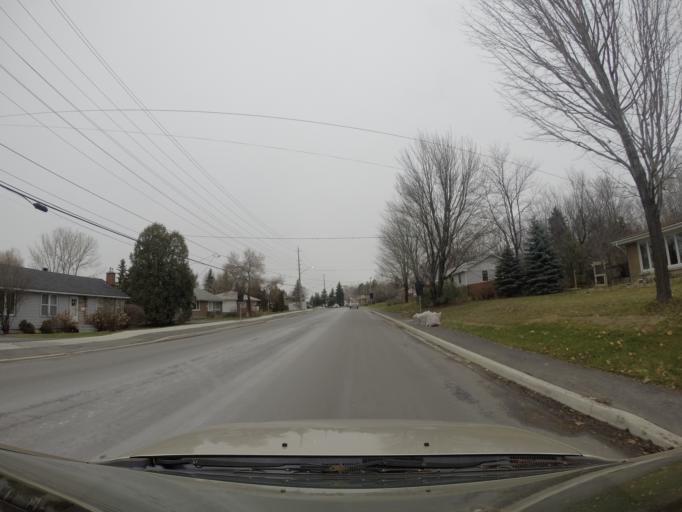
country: CA
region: Ontario
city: Greater Sudbury
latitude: 46.4601
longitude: -81.0176
